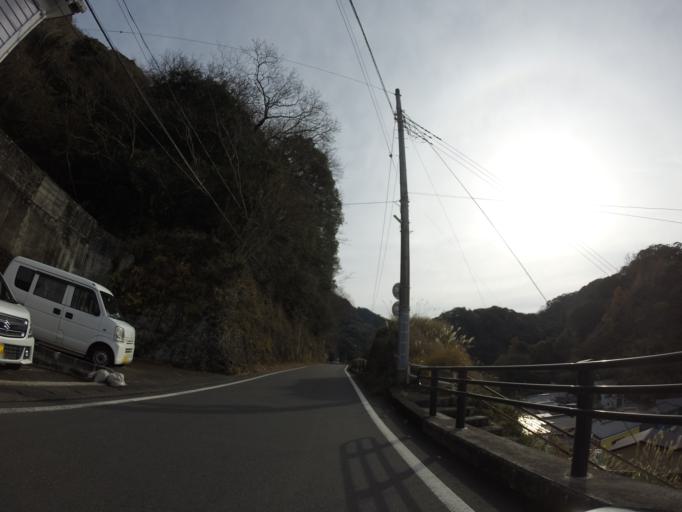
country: JP
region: Shizuoka
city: Heda
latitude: 34.8011
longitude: 138.7643
